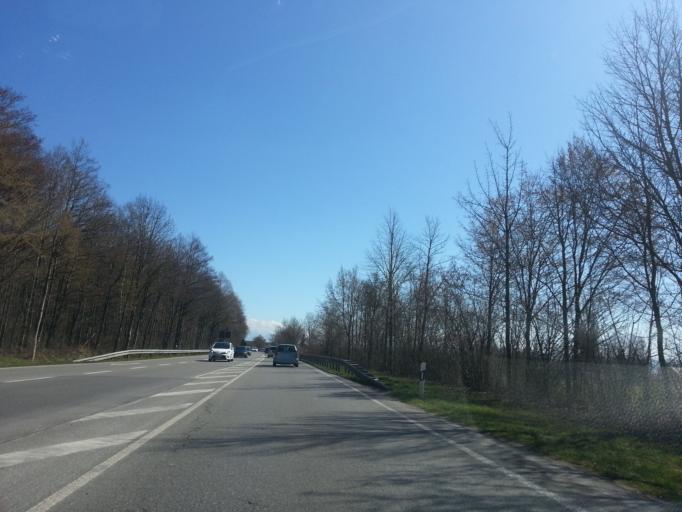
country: DE
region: Baden-Wuerttemberg
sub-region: Tuebingen Region
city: Eriskirch
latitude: 47.6421
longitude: 9.5137
